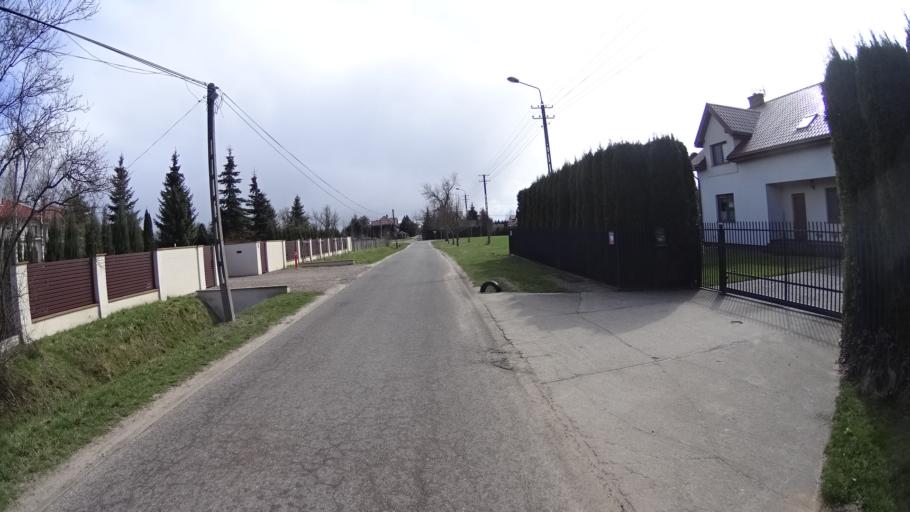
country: PL
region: Masovian Voivodeship
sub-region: Powiat warszawski zachodni
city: Jozefow
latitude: 52.2075
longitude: 20.6830
